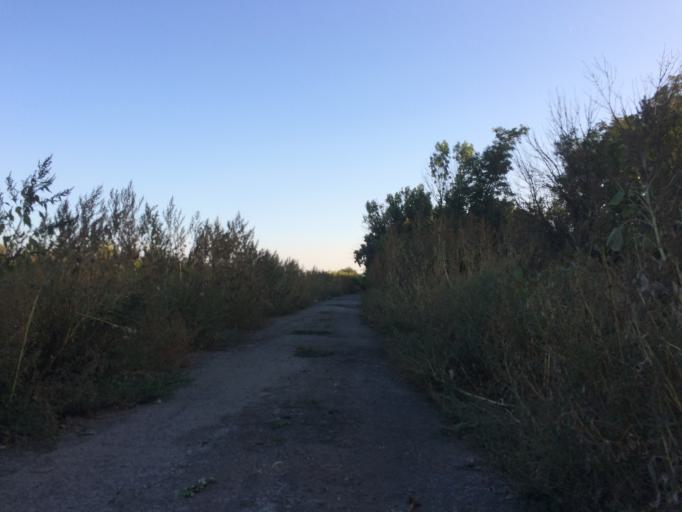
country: RU
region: Rostov
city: Gigant
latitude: 46.5168
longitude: 41.1947
